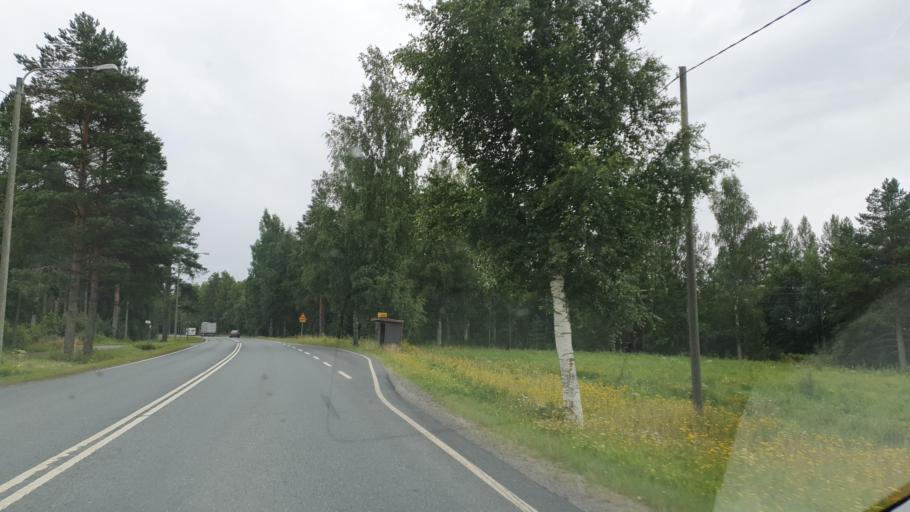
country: FI
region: Northern Savo
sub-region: Kuopio
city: Siilinjaervi
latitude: 63.1272
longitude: 27.6256
